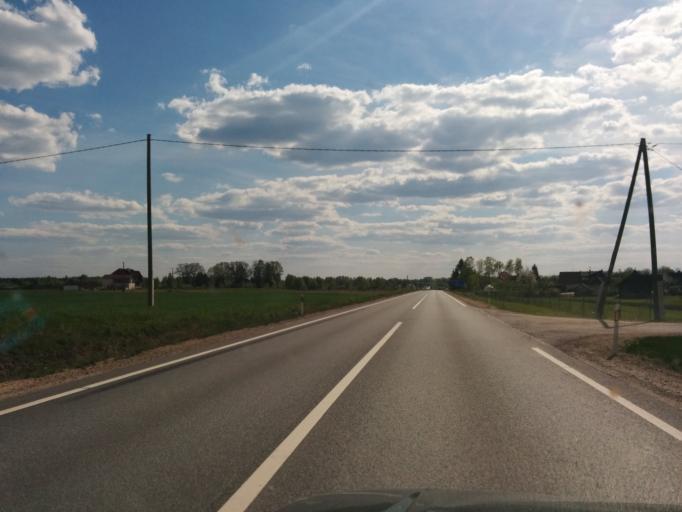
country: LV
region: Krimulda
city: Ragana
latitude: 57.1855
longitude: 24.7227
